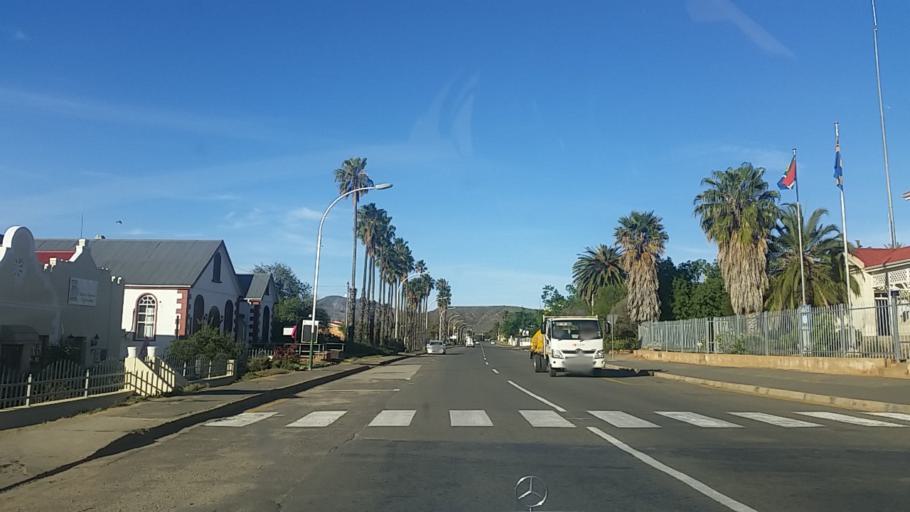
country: ZA
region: Western Cape
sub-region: Eden District Municipality
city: Knysna
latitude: -33.6572
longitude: 23.1254
